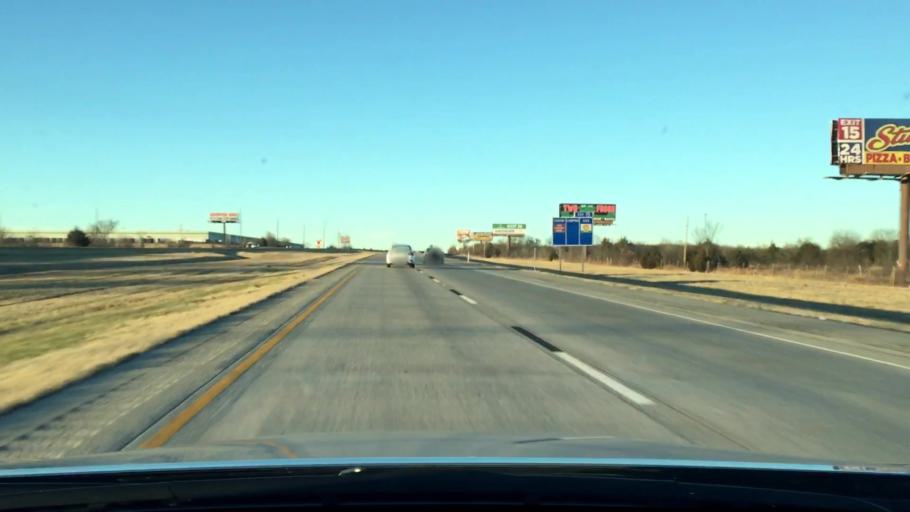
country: US
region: Oklahoma
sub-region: Love County
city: Marietta
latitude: 33.9271
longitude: -97.1343
